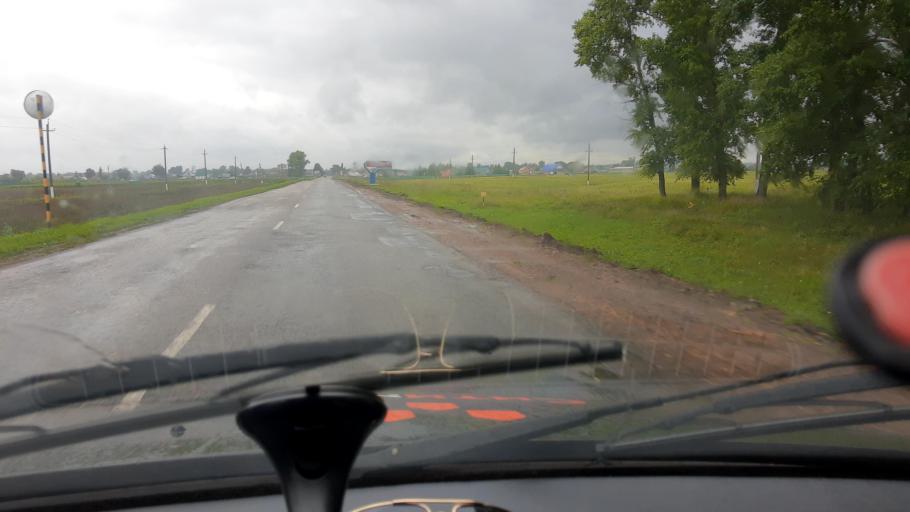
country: RU
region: Bashkortostan
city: Karmaskaly
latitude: 53.9728
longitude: 56.3902
